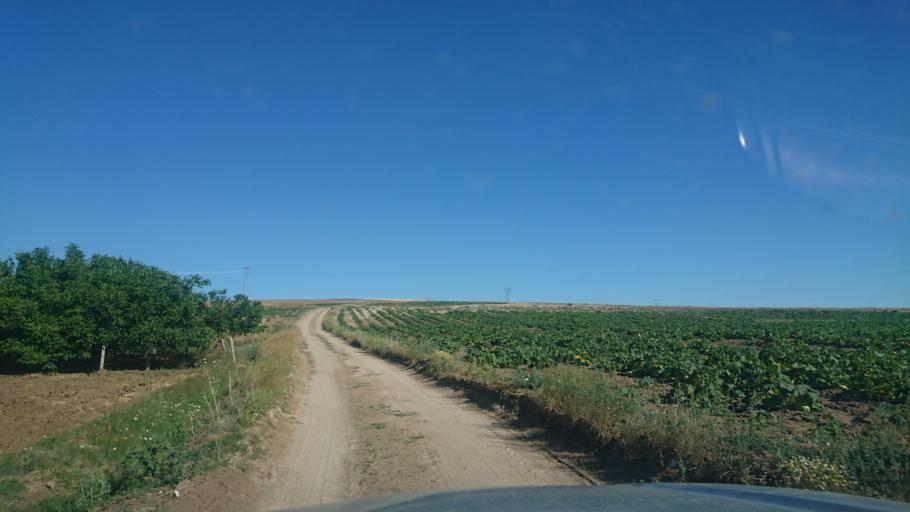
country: TR
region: Aksaray
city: Agacoren
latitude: 38.8318
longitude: 33.9507
